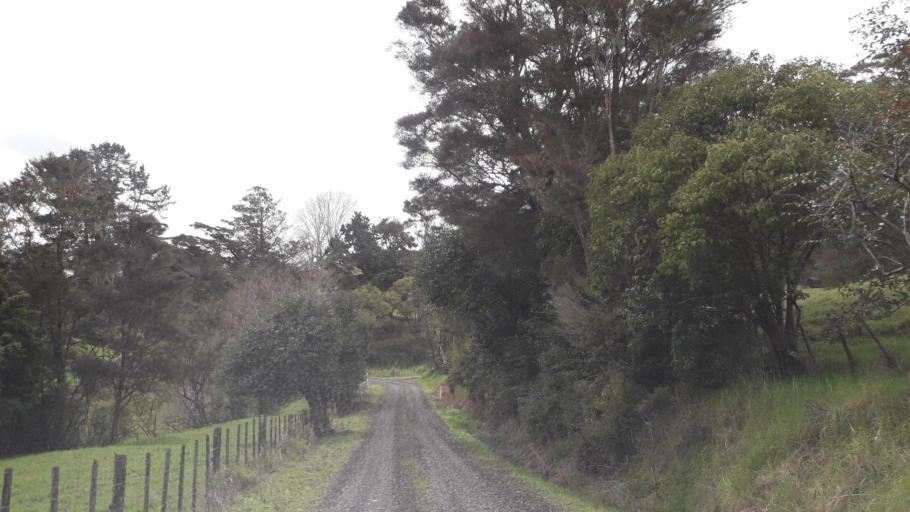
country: NZ
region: Northland
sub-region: Far North District
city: Waimate North
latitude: -35.3164
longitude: 173.5732
